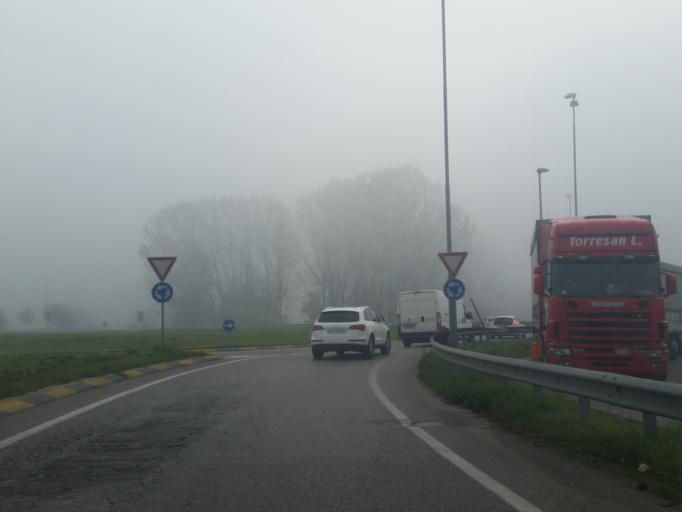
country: IT
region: Lombardy
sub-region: Provincia di Brescia
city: San Paolo
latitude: 45.3821
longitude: 10.0440
